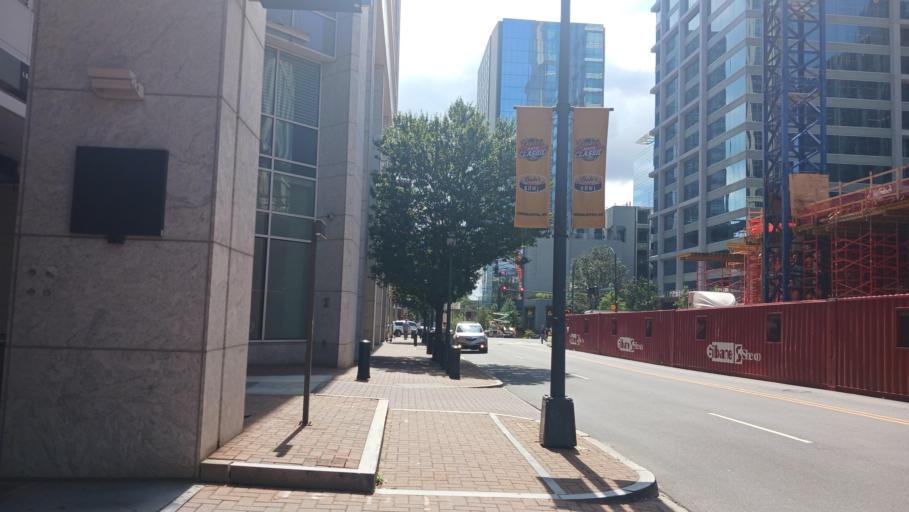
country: US
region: North Carolina
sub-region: Mecklenburg County
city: Charlotte
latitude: 35.2241
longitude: -80.8497
